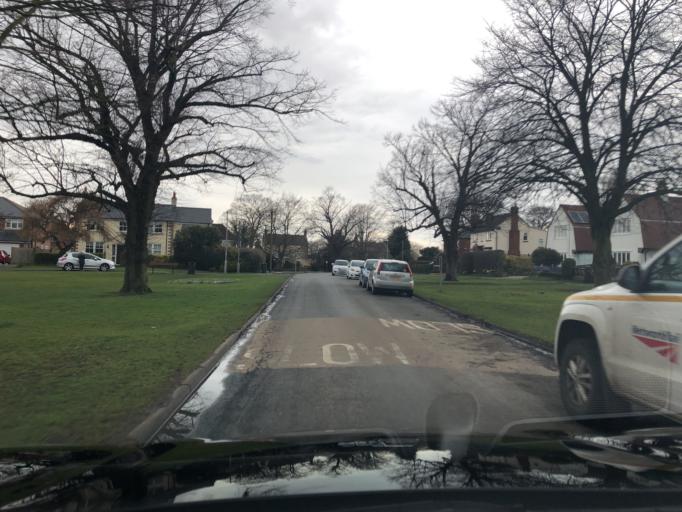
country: GB
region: England
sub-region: North Yorkshire
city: Northallerton
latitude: 54.3347
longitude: -1.4472
